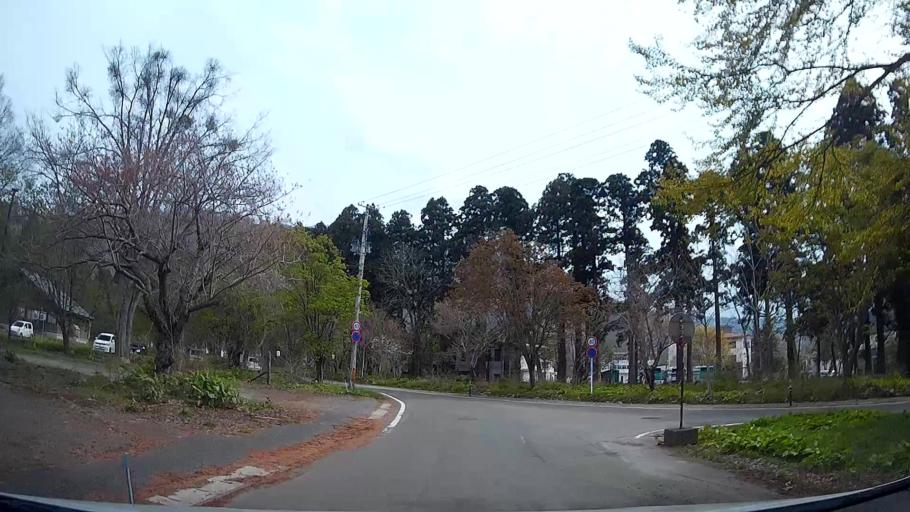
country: JP
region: Akita
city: Hanawa
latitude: 40.4271
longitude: 140.8953
